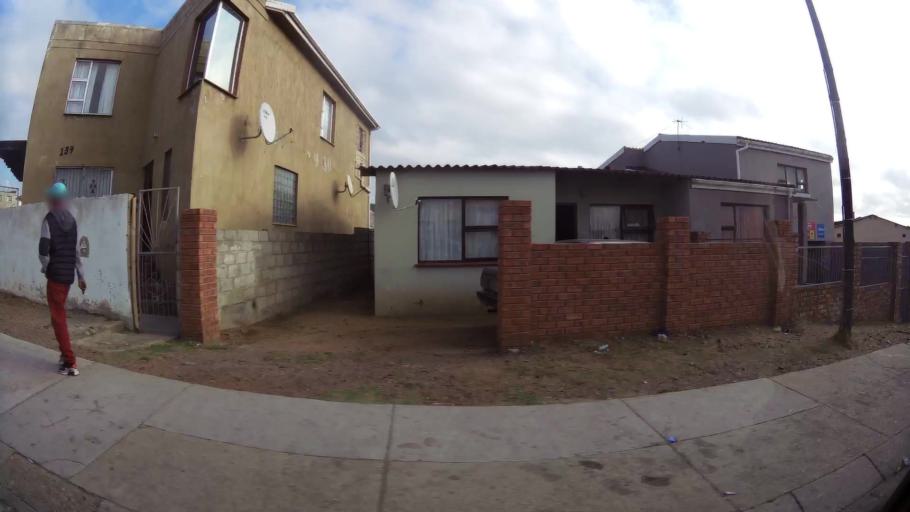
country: ZA
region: Eastern Cape
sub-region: Nelson Mandela Bay Metropolitan Municipality
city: Port Elizabeth
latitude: -33.9164
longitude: 25.5463
